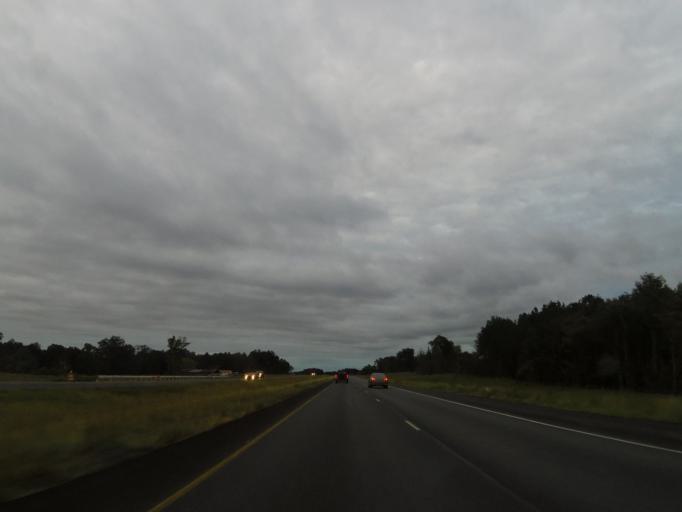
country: US
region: Alabama
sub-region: Saint Clair County
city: Steele
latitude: 33.9458
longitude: -86.1622
